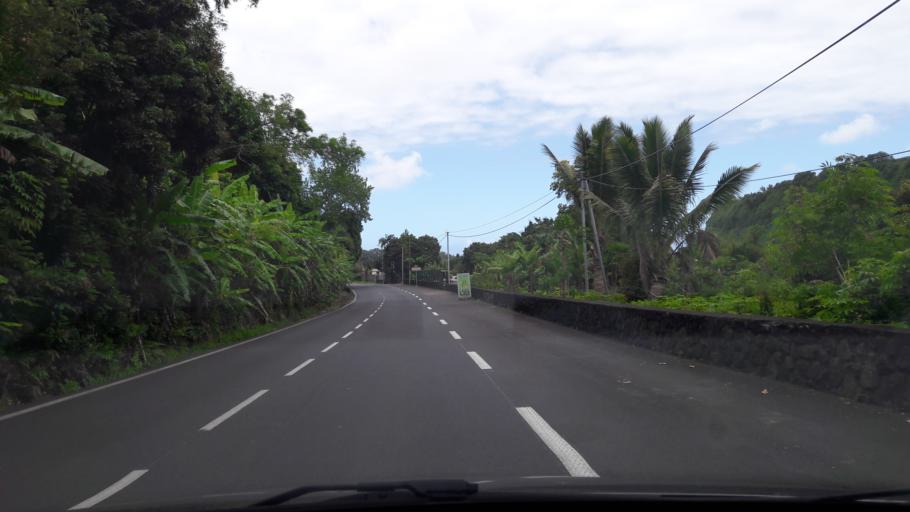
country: RE
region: Reunion
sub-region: Reunion
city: Saint-Andre
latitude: -20.9850
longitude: 55.6257
